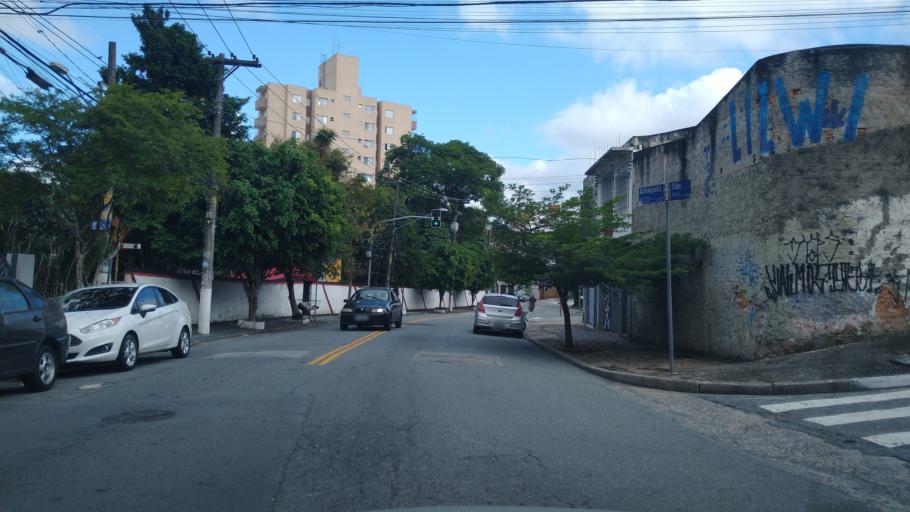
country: BR
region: Sao Paulo
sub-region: Sao Paulo
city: Sao Paulo
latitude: -23.4831
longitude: -46.6196
